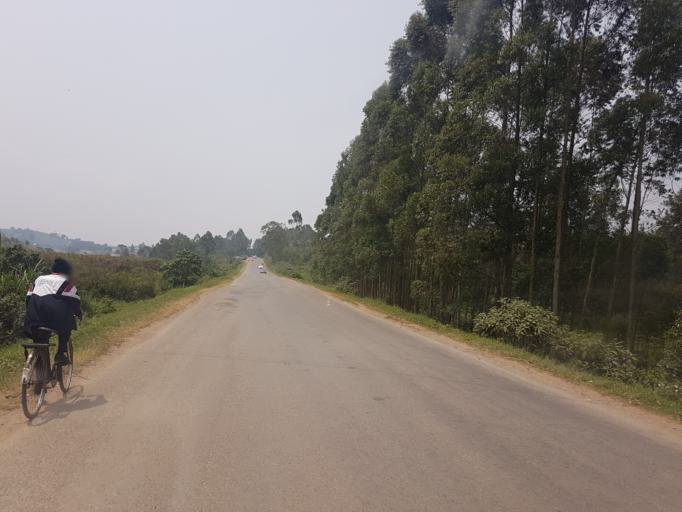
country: UG
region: Western Region
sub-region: Bushenyi District
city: Bushenyi
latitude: -0.5406
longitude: 30.1513
